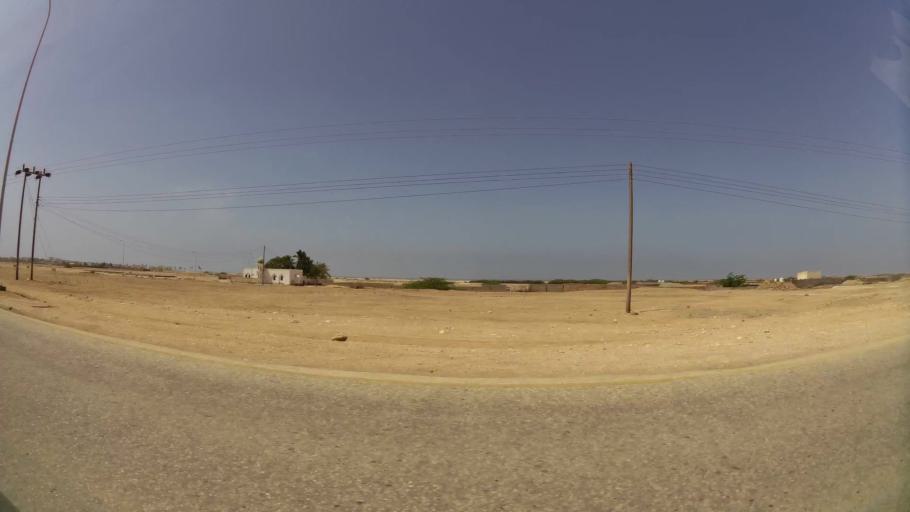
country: OM
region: Zufar
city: Salalah
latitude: 17.0374
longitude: 54.2864
